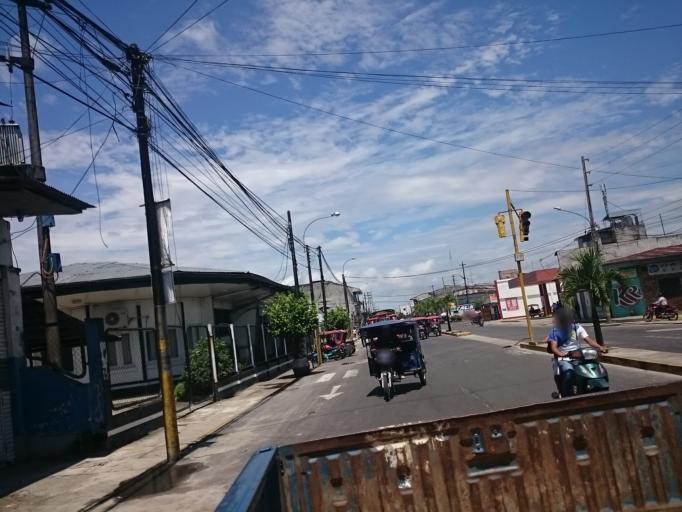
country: PE
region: Loreto
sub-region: Provincia de Maynas
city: Iquitos
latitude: -3.7393
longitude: -73.2410
